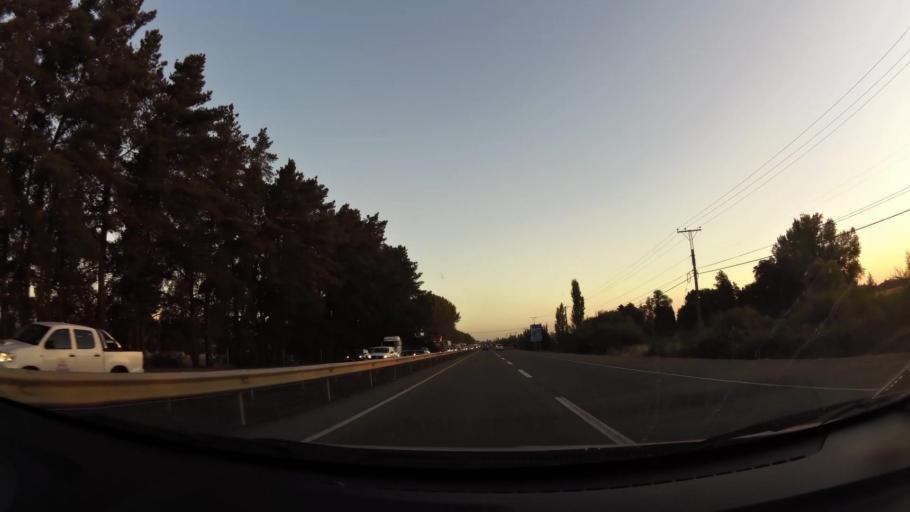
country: CL
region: Maule
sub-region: Provincia de Linares
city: Linares
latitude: -35.7523
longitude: -71.6731
